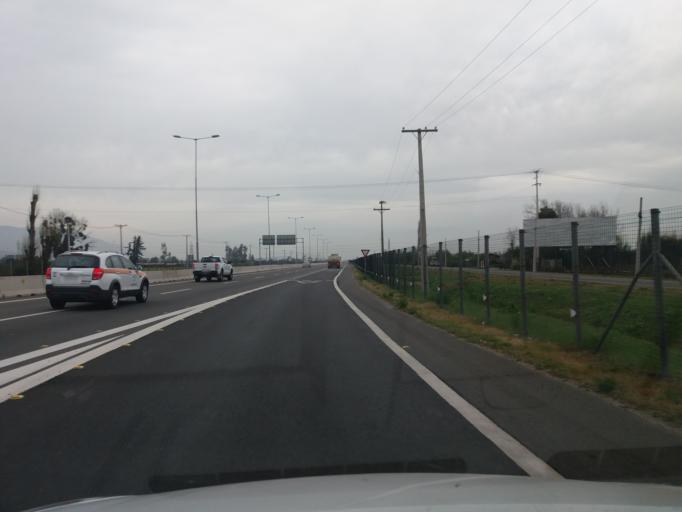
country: CL
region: Valparaiso
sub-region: Provincia de Quillota
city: Quillota
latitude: -32.9256
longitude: -71.2822
